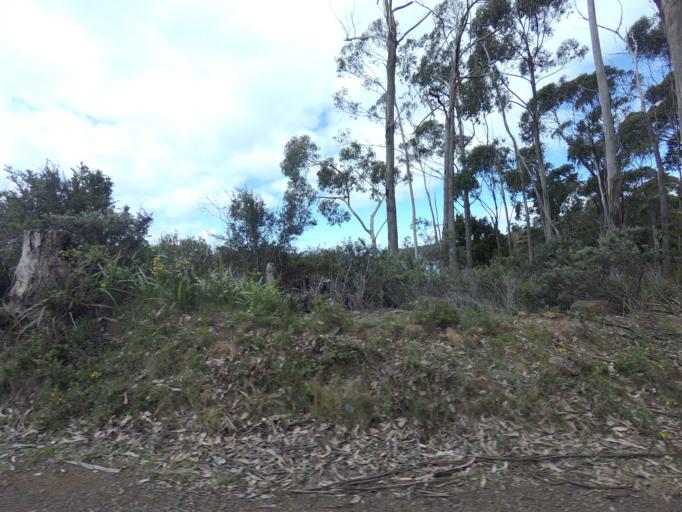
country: AU
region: Tasmania
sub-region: Huon Valley
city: Geeveston
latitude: -43.4213
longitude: 147.0122
